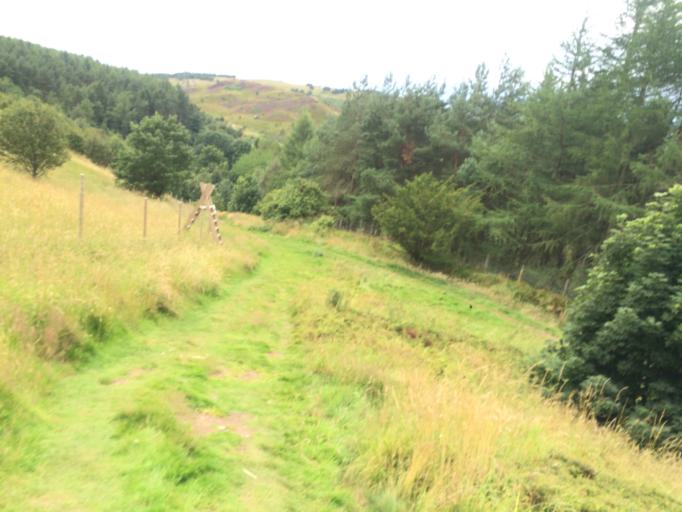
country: GB
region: Scotland
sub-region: Edinburgh
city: Colinton
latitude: 55.8931
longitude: -3.2587
